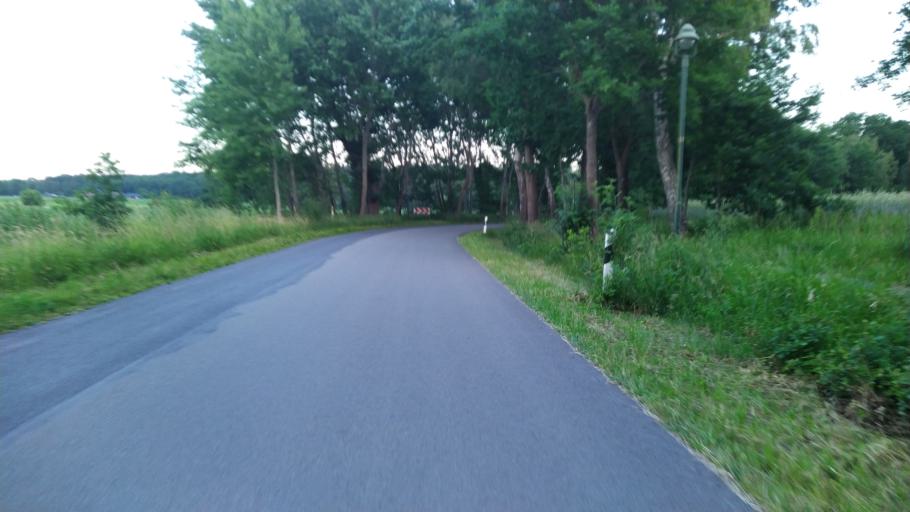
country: DE
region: Lower Saxony
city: Bremervorde
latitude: 53.4851
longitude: 9.1877
